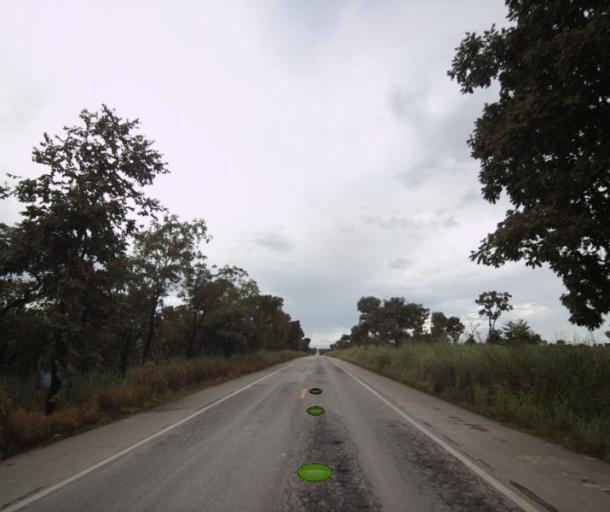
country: BR
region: Goias
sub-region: Porangatu
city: Porangatu
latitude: -13.5884
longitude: -49.0416
